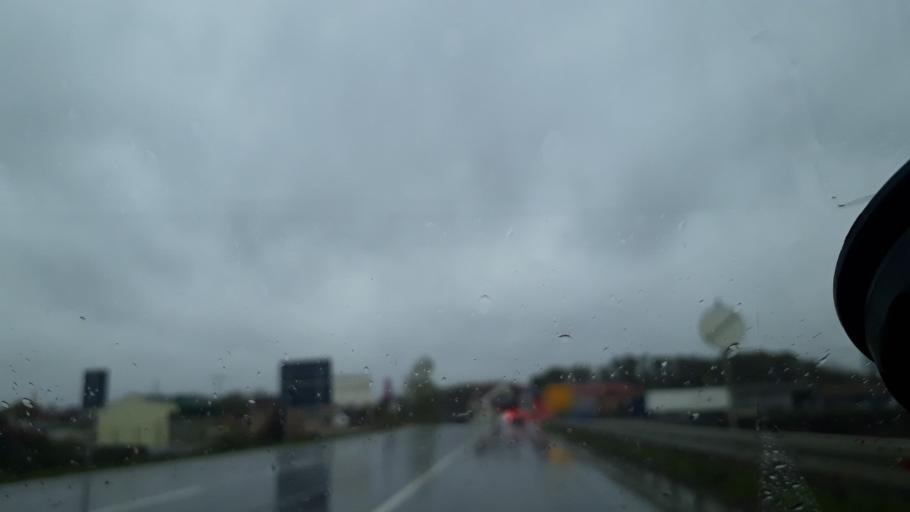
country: BA
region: Republika Srpska
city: Prnjavor
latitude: 44.8550
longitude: 17.6891
